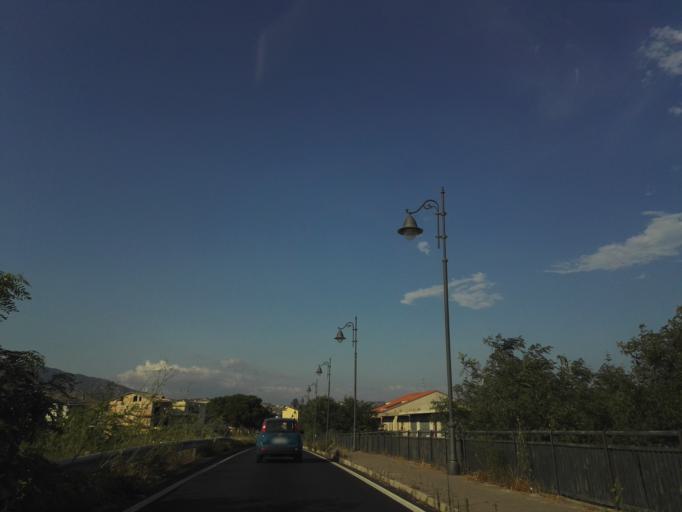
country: IT
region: Calabria
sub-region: Provincia di Reggio Calabria
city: Marina di Gioiosa Ionica
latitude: 38.2965
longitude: 16.3241
